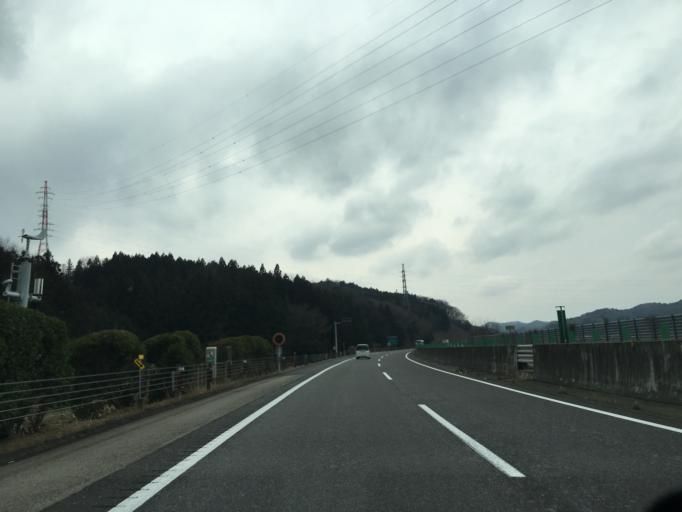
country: JP
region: Fukushima
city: Sukagawa
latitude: 37.1435
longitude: 140.2302
